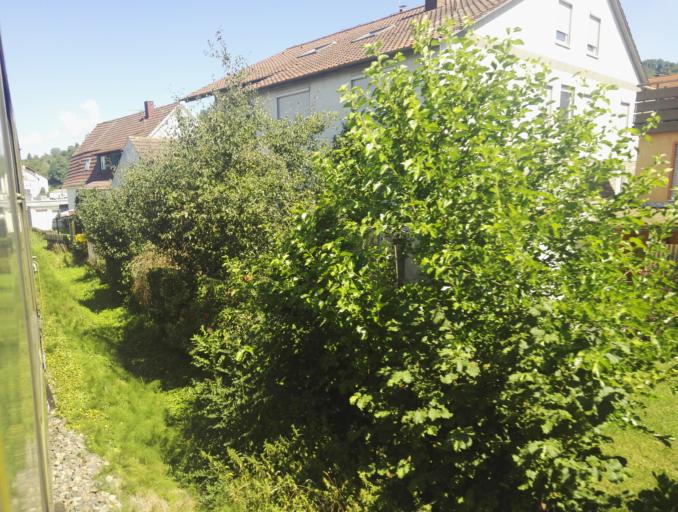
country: DE
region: Baden-Wuerttemberg
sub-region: Regierungsbezirk Stuttgart
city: Urbach
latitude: 48.8323
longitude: 9.5491
